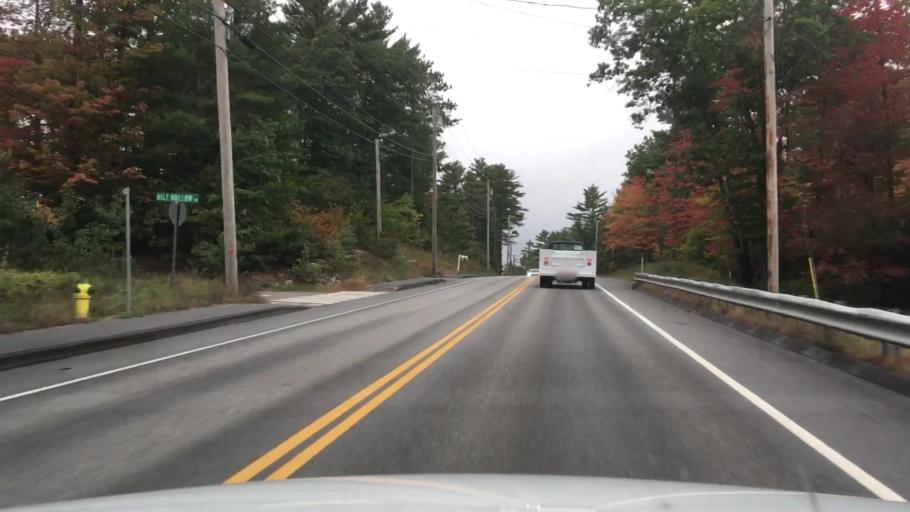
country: US
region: Maine
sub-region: Androscoggin County
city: Poland
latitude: 44.0656
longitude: -70.3996
